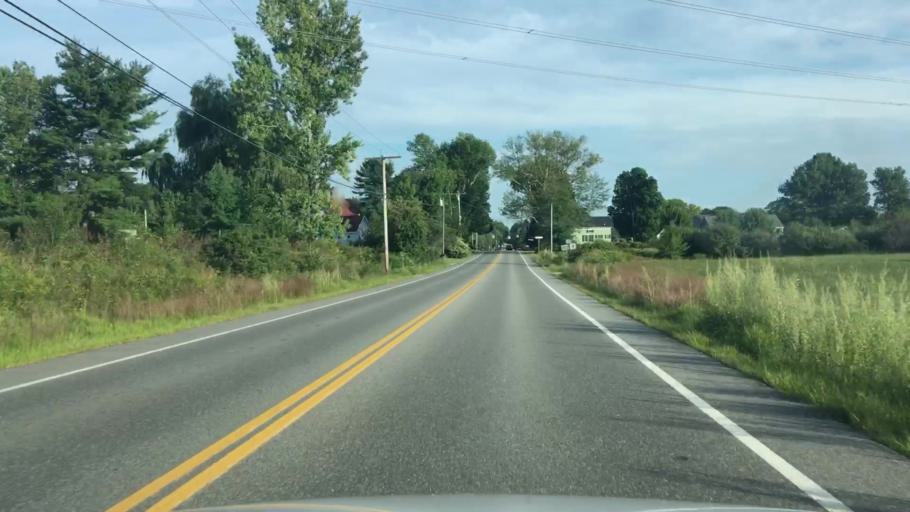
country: US
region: Maine
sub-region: Cumberland County
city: South Windham
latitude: 43.7474
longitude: -70.4275
